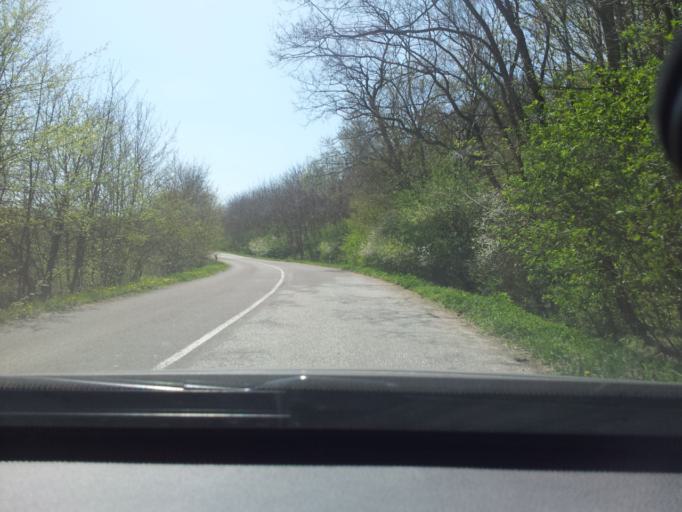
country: SK
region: Nitriansky
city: Tlmace
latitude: 48.2967
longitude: 18.4502
